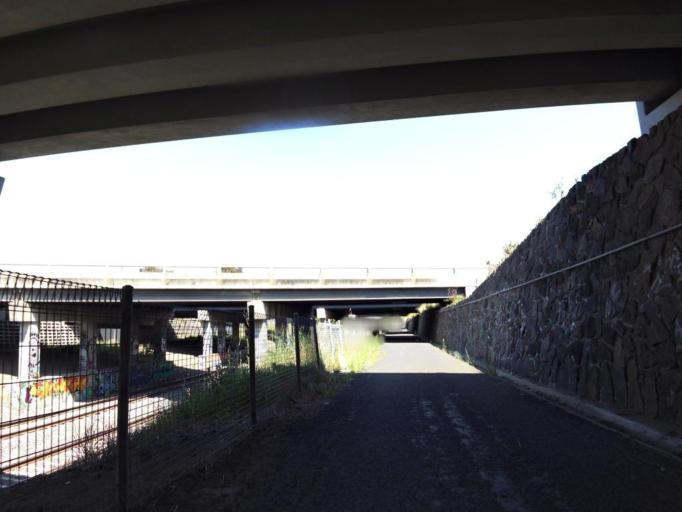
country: AU
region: Victoria
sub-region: Moonee Valley
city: Keilor East
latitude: -37.7278
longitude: 144.8641
